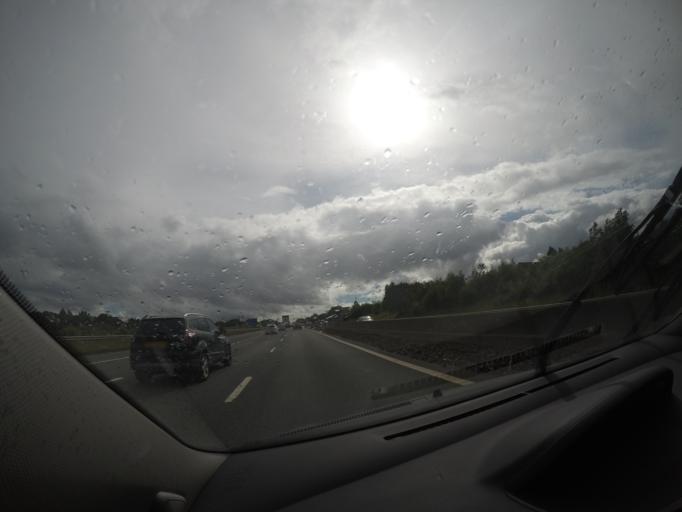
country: GB
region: Scotland
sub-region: North Lanarkshire
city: Cumbernauld
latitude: 55.9773
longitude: -3.9485
